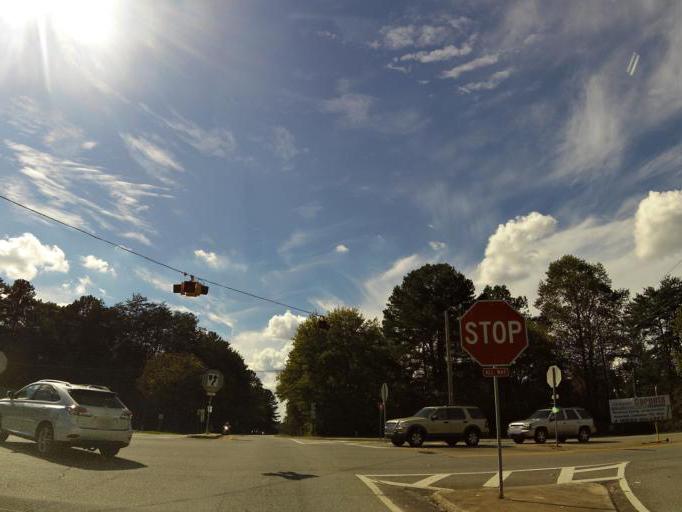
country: US
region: Georgia
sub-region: Pickens County
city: Nelson
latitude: 34.4134
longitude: -84.3890
